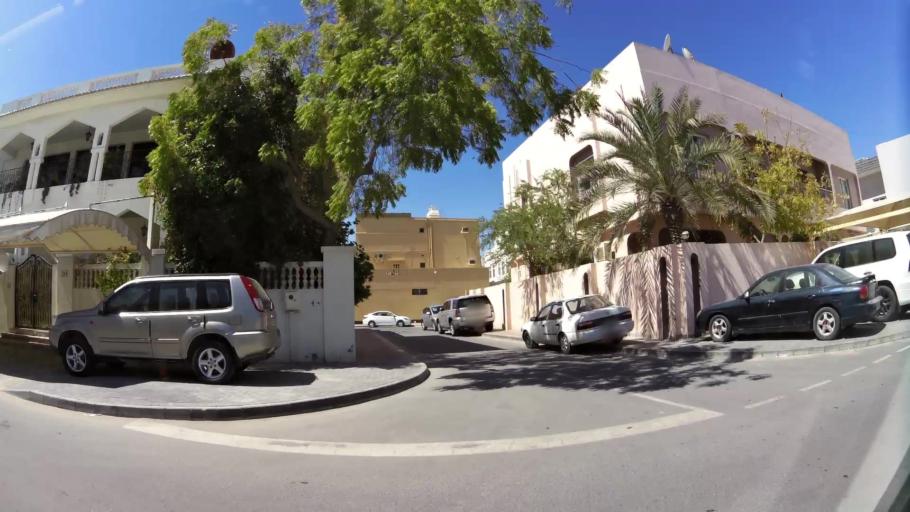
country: BH
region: Muharraq
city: Al Muharraq
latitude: 26.2693
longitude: 50.6059
